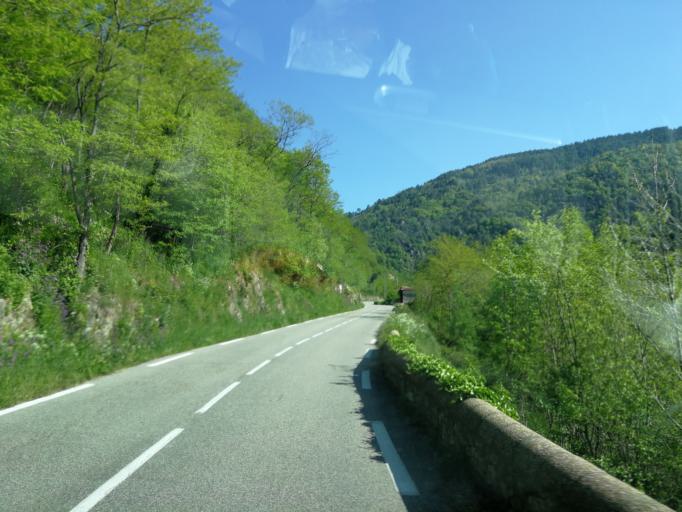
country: FR
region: Rhone-Alpes
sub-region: Departement de l'Ardeche
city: Saint-Sauveur-de-Montagut
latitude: 44.8318
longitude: 4.5755
